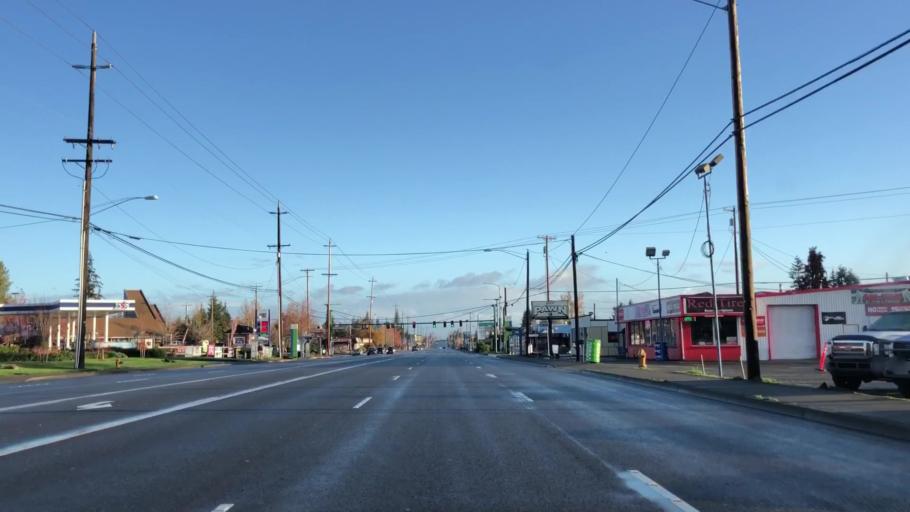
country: US
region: Washington
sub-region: Snohomish County
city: Martha Lake
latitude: 47.9090
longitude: -122.2400
